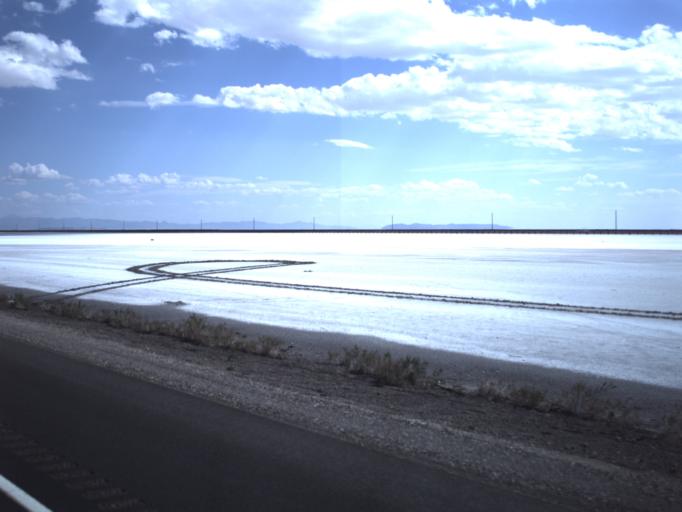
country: US
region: Utah
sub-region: Tooele County
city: Wendover
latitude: 40.7342
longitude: -113.6447
